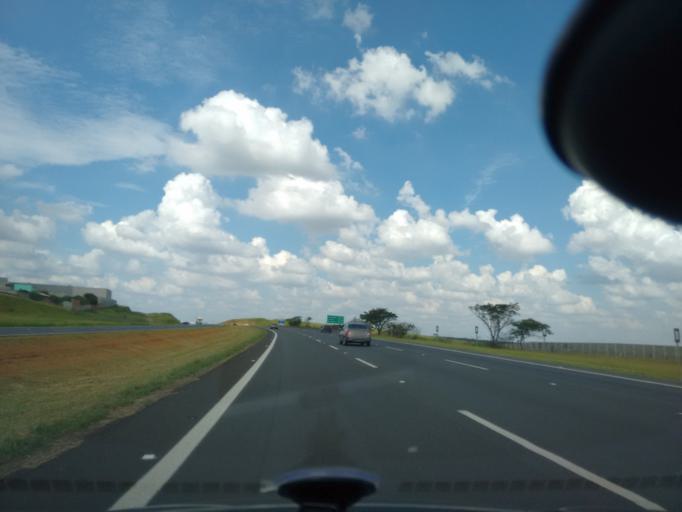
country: BR
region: Sao Paulo
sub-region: Hortolandia
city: Hortolandia
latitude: -22.9122
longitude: -47.1904
